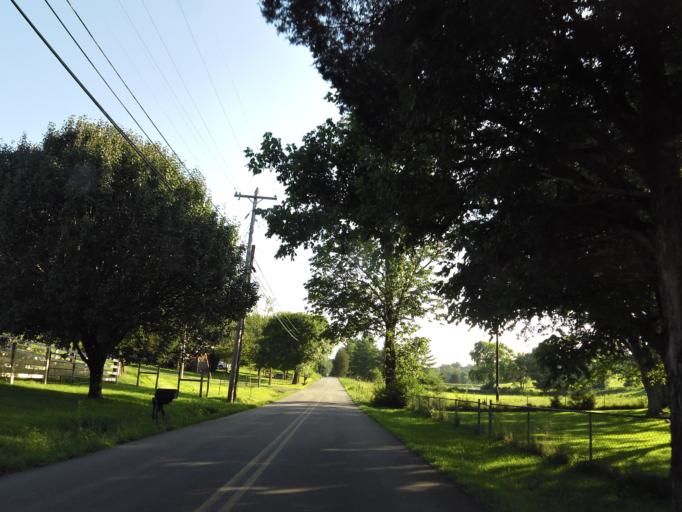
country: US
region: Tennessee
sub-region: Blount County
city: Maryville
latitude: 35.7261
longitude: -83.9056
